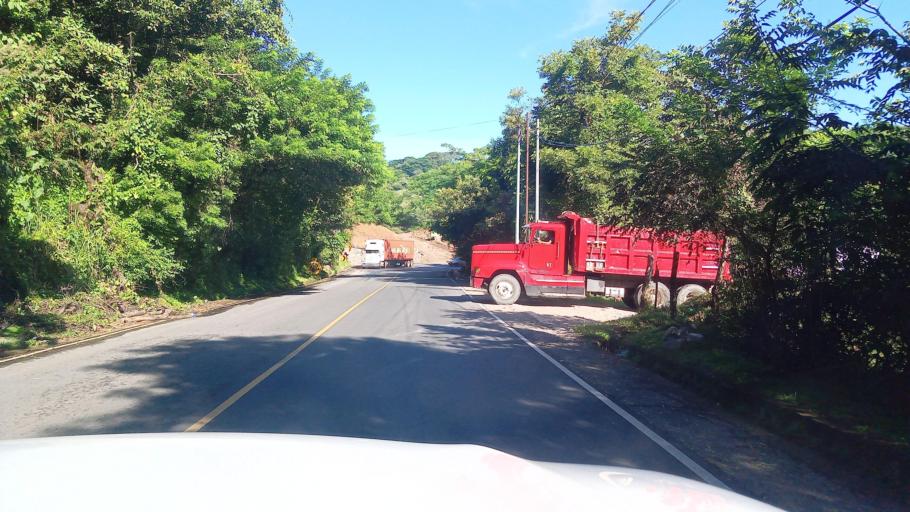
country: HN
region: Ocotepeque
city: Antigua Ocotepeque
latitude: 14.3217
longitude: -89.1770
